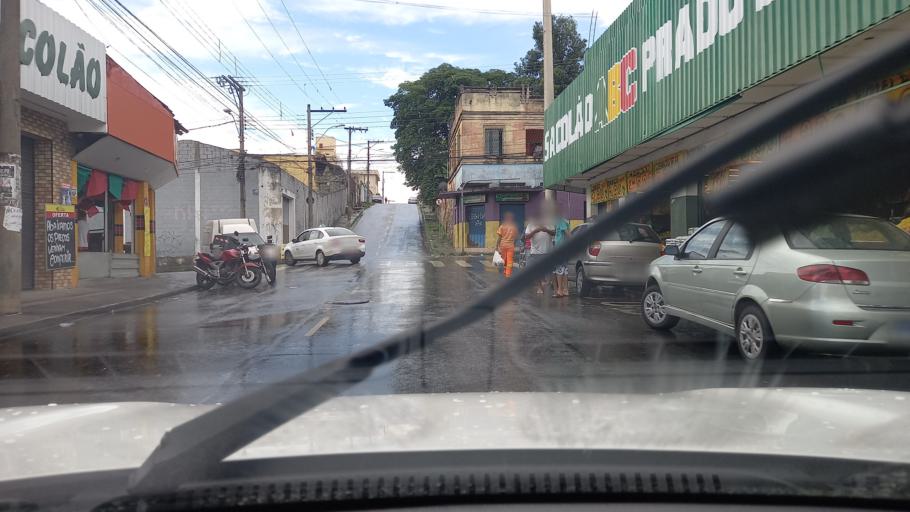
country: BR
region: Minas Gerais
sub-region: Belo Horizonte
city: Belo Horizonte
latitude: -19.9017
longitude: -43.9522
